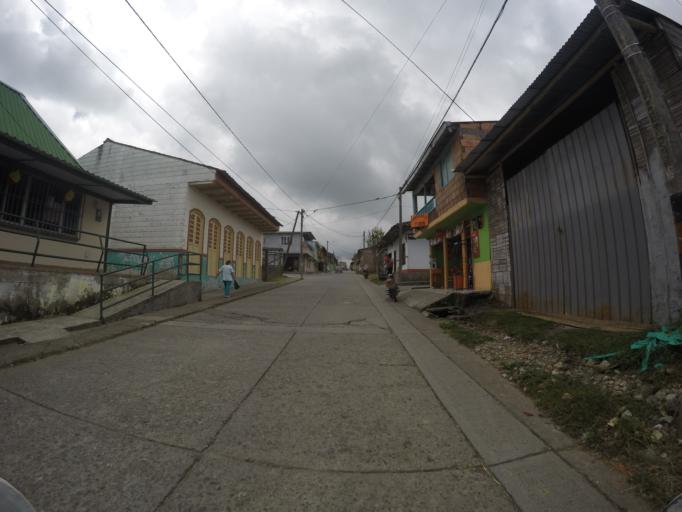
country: CO
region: Quindio
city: Filandia
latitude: 4.6717
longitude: -75.6609
